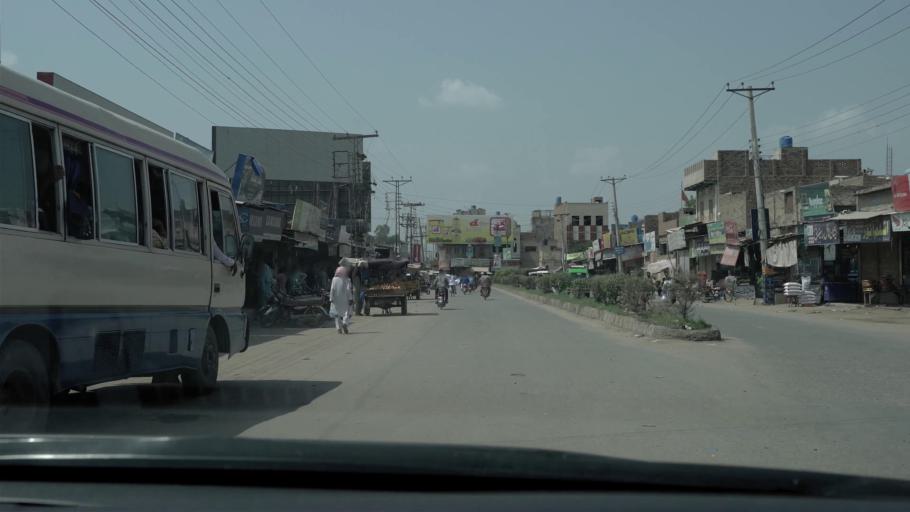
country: PK
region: Punjab
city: Gojra
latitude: 31.1511
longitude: 72.6792
